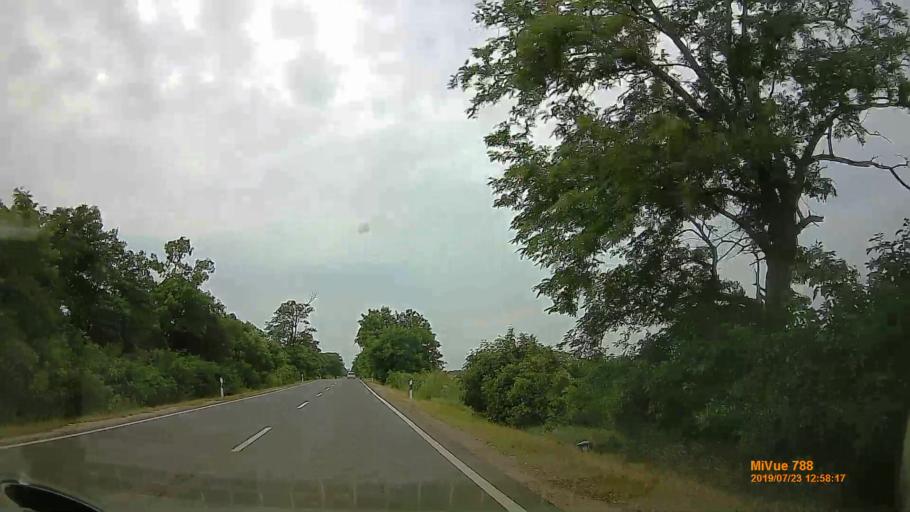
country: HU
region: Szabolcs-Szatmar-Bereg
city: Nagycserkesz
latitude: 47.9588
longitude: 21.4600
